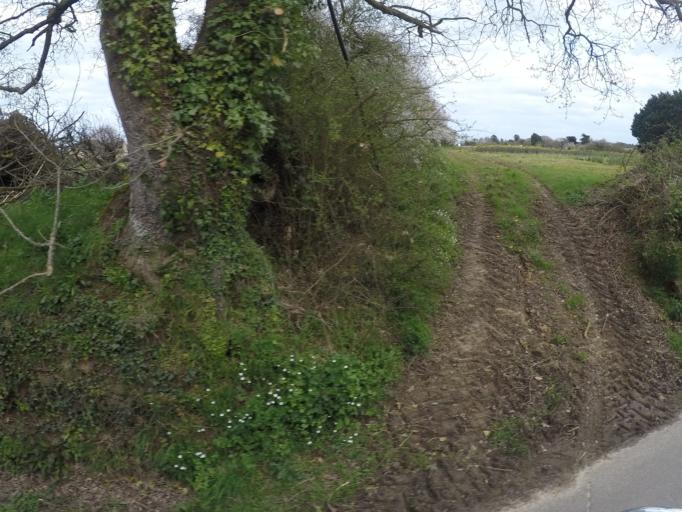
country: FR
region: Brittany
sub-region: Departement des Cotes-d'Armor
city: Plouha
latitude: 48.7071
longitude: -2.9372
